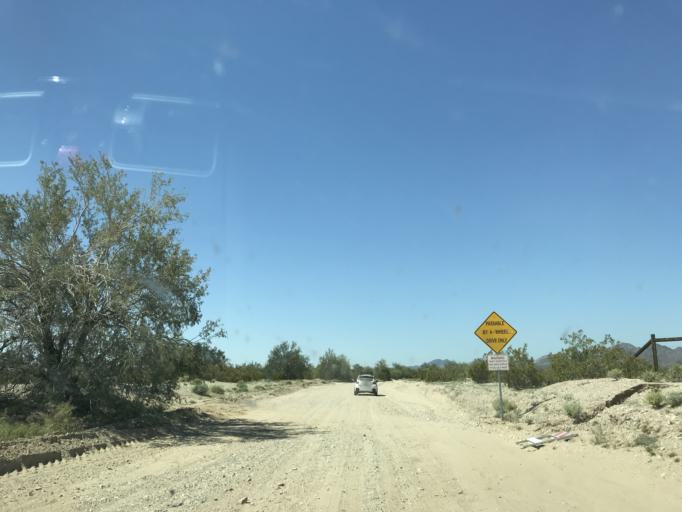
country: US
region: California
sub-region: Riverside County
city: Mesa Verde
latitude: 33.4908
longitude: -114.8881
